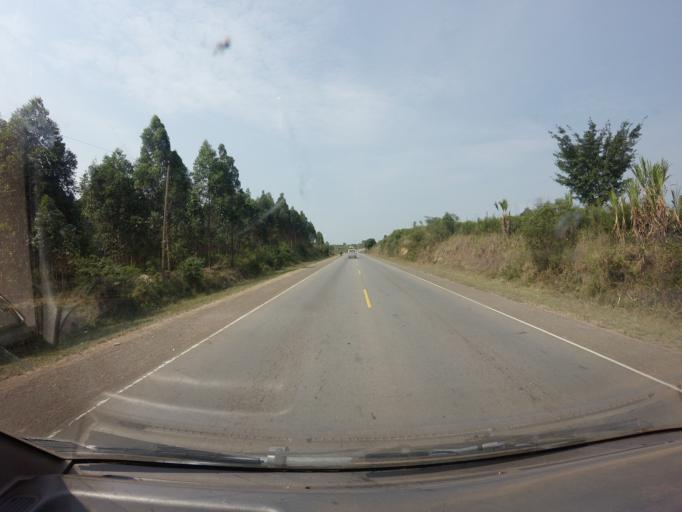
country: UG
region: Central Region
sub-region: Lwengo District
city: Lwengo
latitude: -0.3999
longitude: 31.3951
